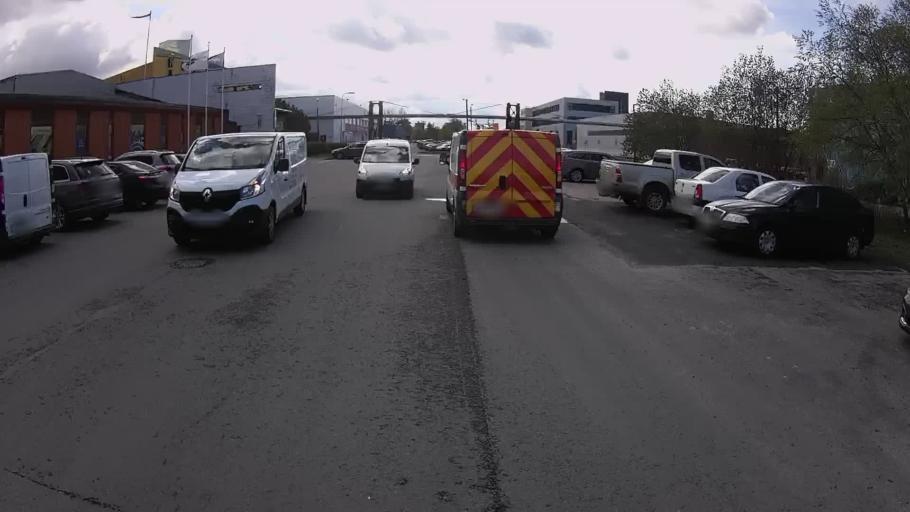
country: EE
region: Harju
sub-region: Tallinna linn
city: Tallinn
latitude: 59.4215
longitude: 24.6853
